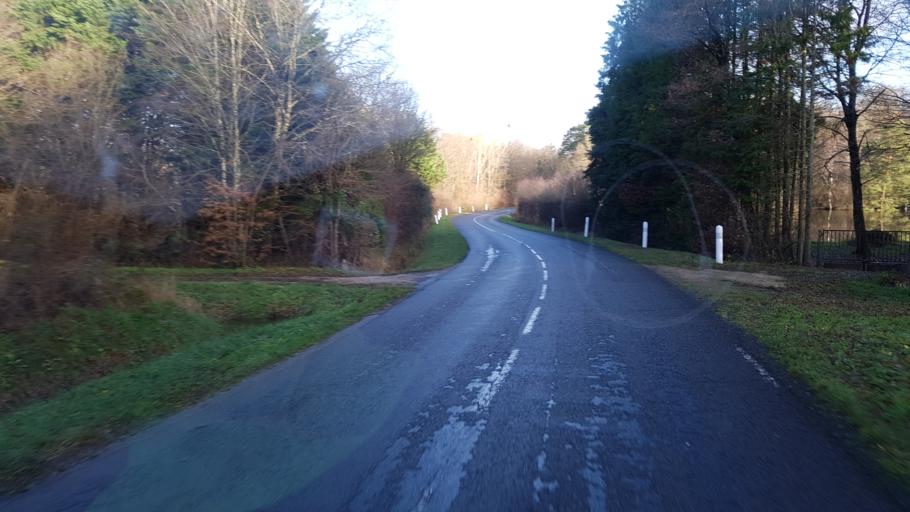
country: FR
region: Centre
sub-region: Departement du Loiret
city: Chilleurs-aux-Bois
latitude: 48.0572
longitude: 2.2213
